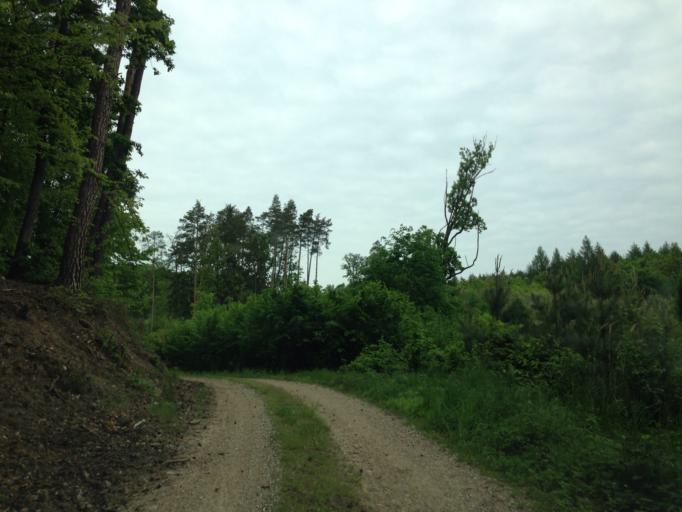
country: PL
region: Kujawsko-Pomorskie
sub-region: Powiat brodnicki
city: Gorzno
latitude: 53.2610
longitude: 19.7121
